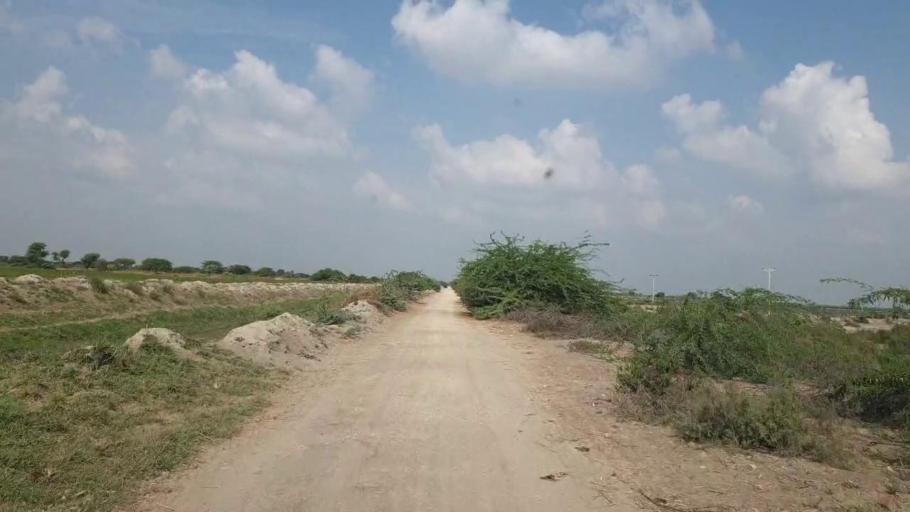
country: PK
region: Sindh
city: Badin
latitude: 24.5010
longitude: 68.6557
